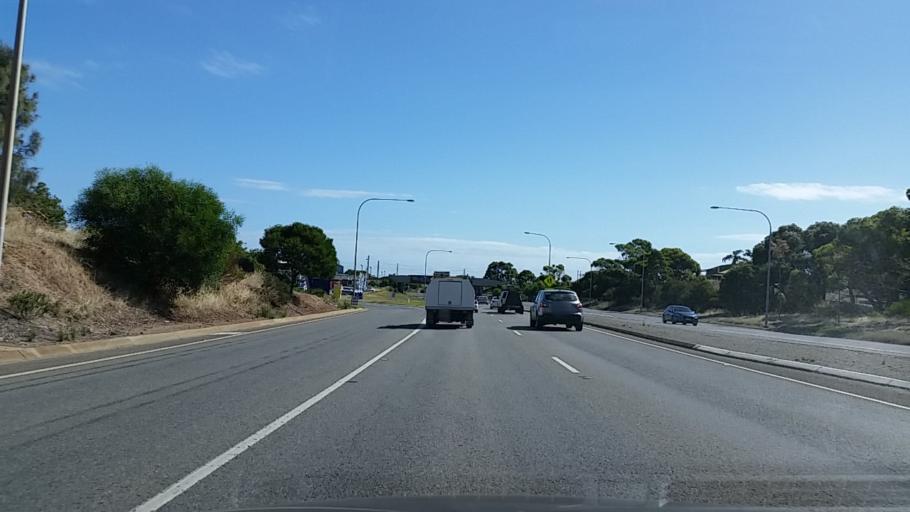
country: AU
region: South Australia
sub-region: Onkaparinga
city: Morphett Vale
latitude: -35.1095
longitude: 138.4960
